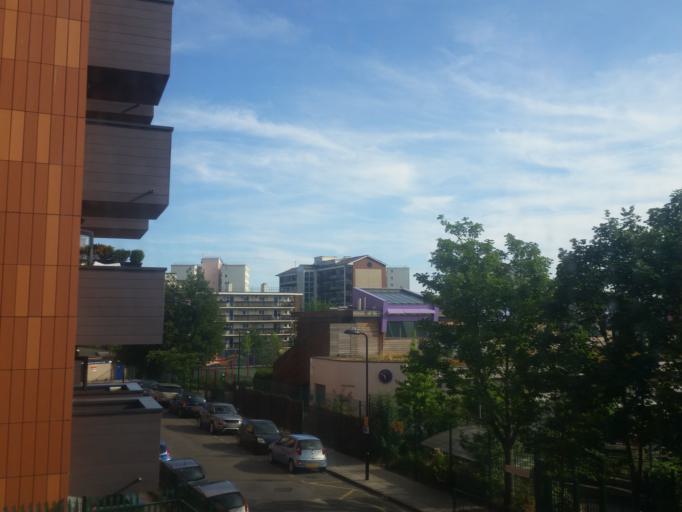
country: GB
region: England
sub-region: Greater London
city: Hackney
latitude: 51.5470
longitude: -0.0442
